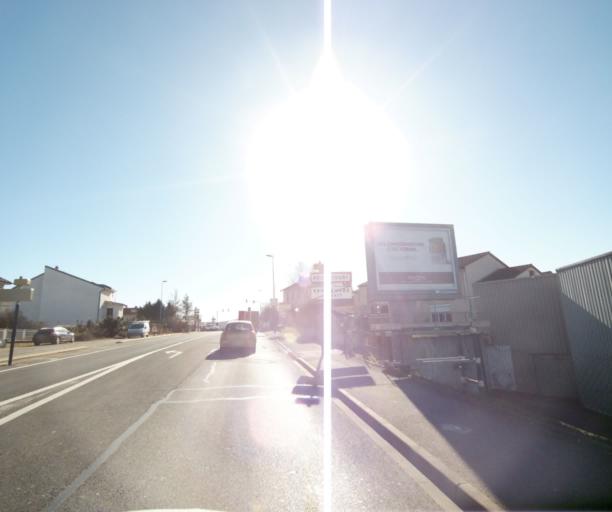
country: FR
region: Lorraine
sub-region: Departement de Meurthe-et-Moselle
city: Vandoeuvre-les-Nancy
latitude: 48.6535
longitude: 6.1854
